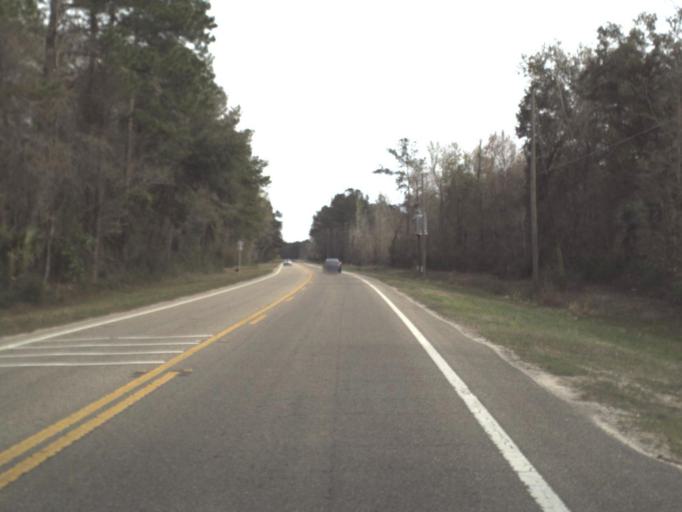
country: US
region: Florida
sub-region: Leon County
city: Woodville
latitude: 30.2313
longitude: -84.2275
